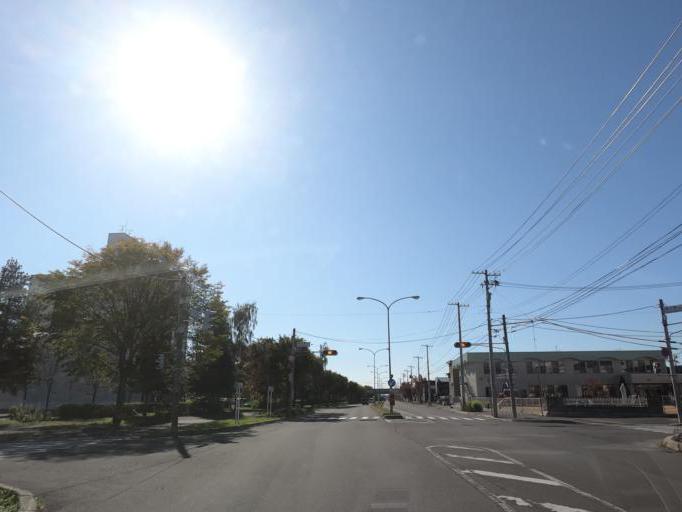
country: JP
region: Hokkaido
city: Obihiro
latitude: 42.9177
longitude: 143.2123
